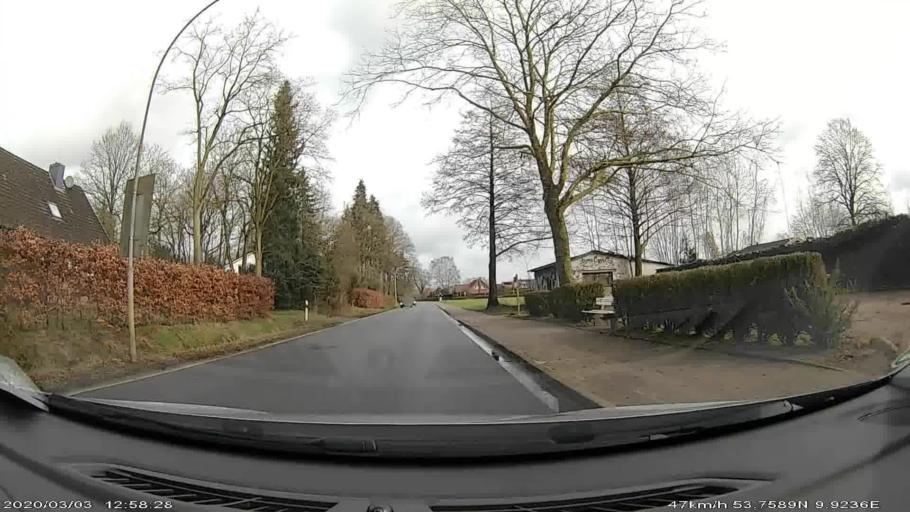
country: DE
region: Schleswig-Holstein
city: Ellerau
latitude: 53.7593
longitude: 9.9252
